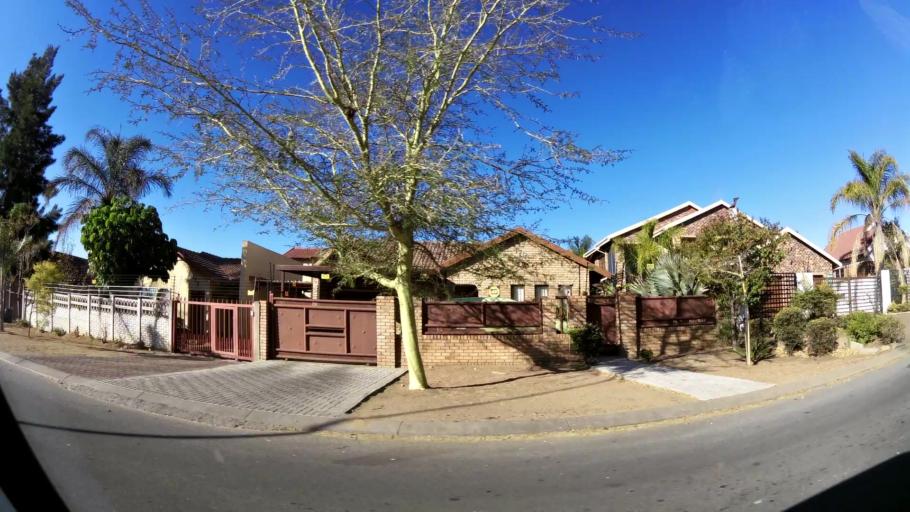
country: ZA
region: Limpopo
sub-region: Capricorn District Municipality
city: Polokwane
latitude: -23.8825
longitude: 29.4739
